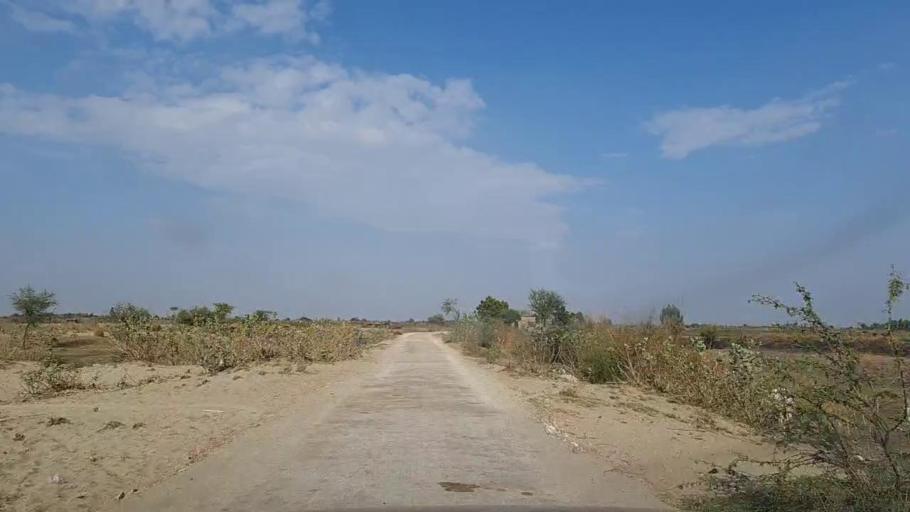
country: PK
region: Sindh
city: Sanghar
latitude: 26.2624
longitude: 69.0088
